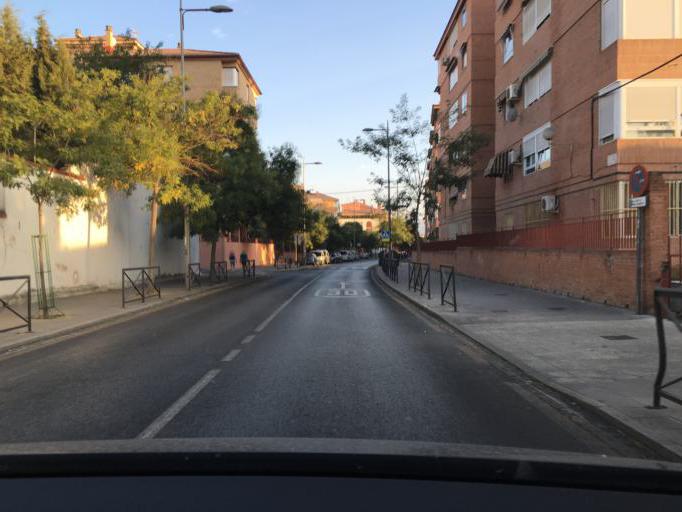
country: ES
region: Andalusia
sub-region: Provincia de Granada
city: Granada
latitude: 37.1920
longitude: -3.6040
